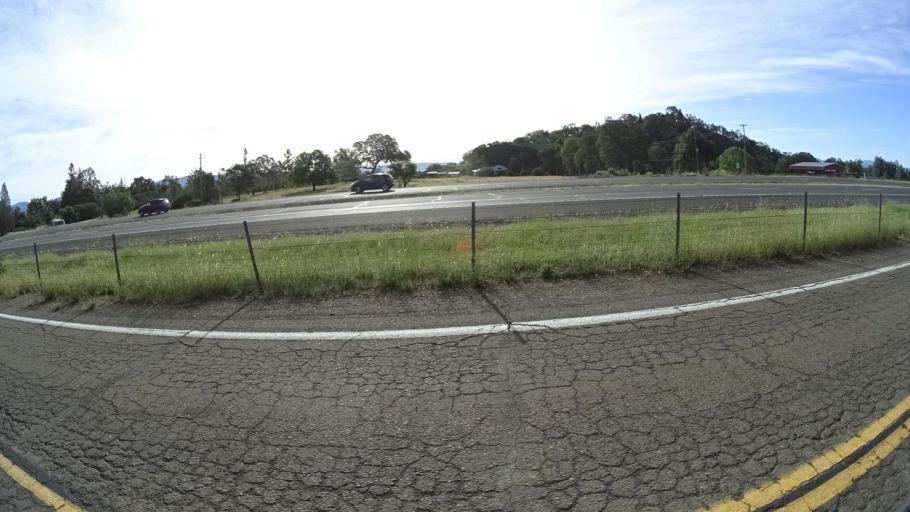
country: US
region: California
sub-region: Lake County
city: North Lakeport
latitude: 39.0738
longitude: -122.9314
